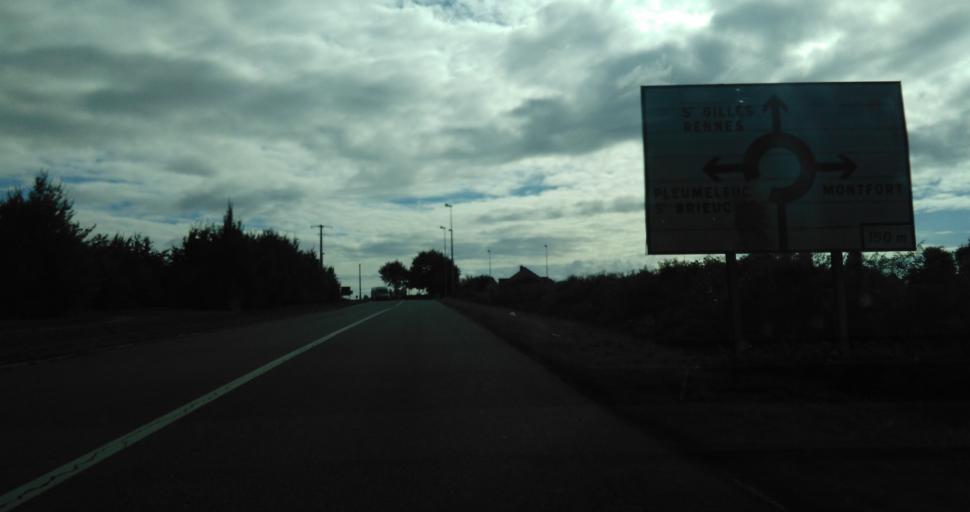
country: FR
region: Brittany
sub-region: Departement d'Ille-et-Vilaine
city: Pleumeleuc
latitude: 48.1766
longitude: -1.9279
